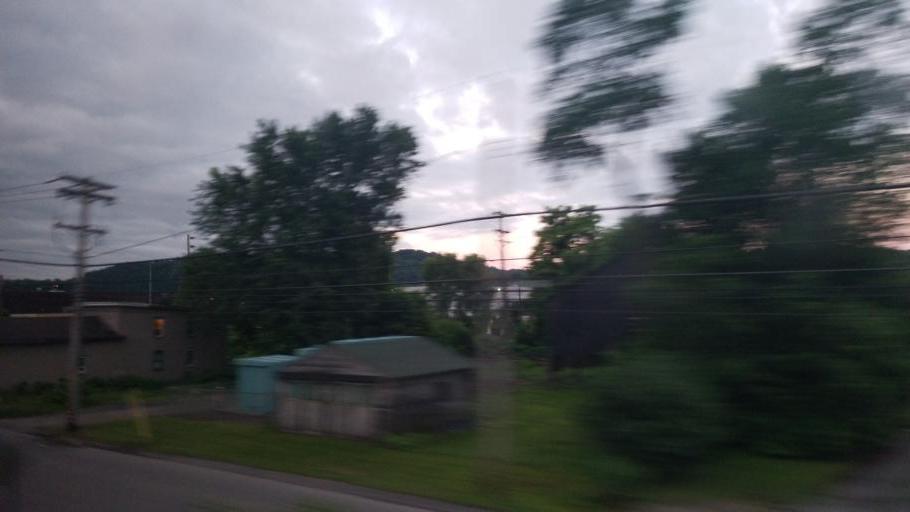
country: US
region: Pennsylvania
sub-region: Allegheny County
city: Leetsdale
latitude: 40.5636
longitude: -80.2092
